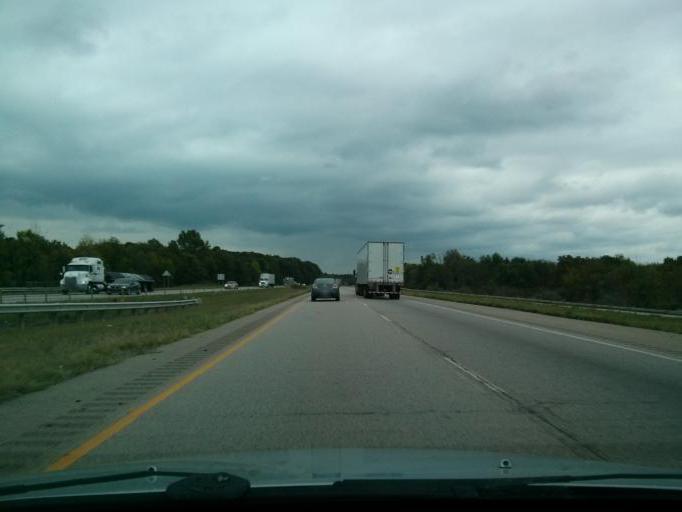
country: US
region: Ohio
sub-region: Mahoning County
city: Craig Beach
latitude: 41.1058
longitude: -81.0508
